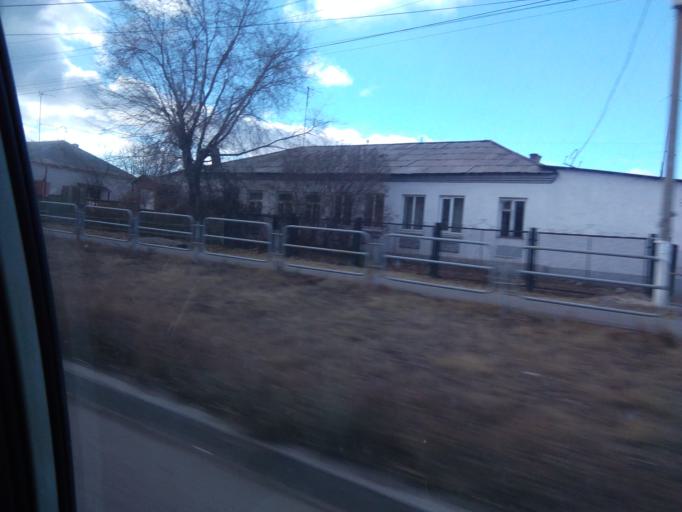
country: RU
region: Chelyabinsk
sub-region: Gorod Magnitogorsk
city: Magnitogorsk
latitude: 53.3910
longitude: 59.0519
